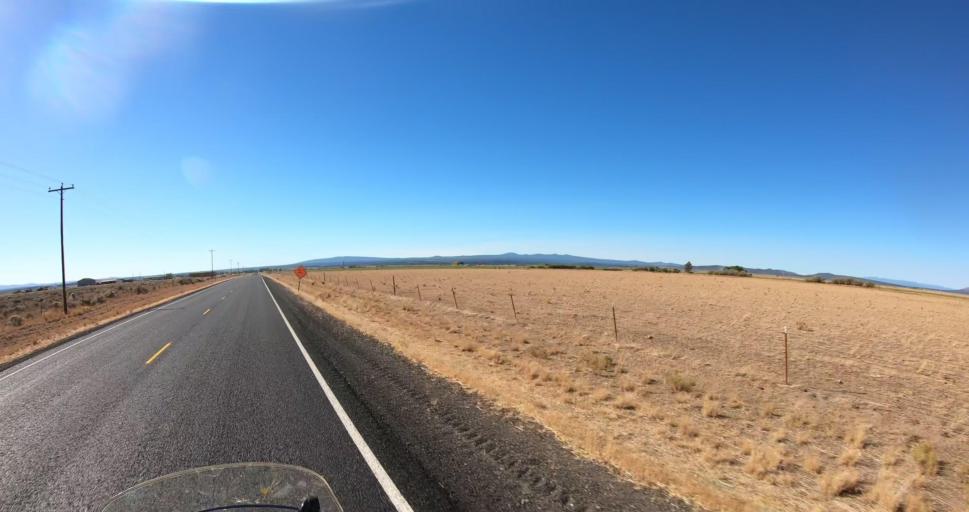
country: US
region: Oregon
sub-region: Deschutes County
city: La Pine
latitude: 43.1276
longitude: -121.0108
